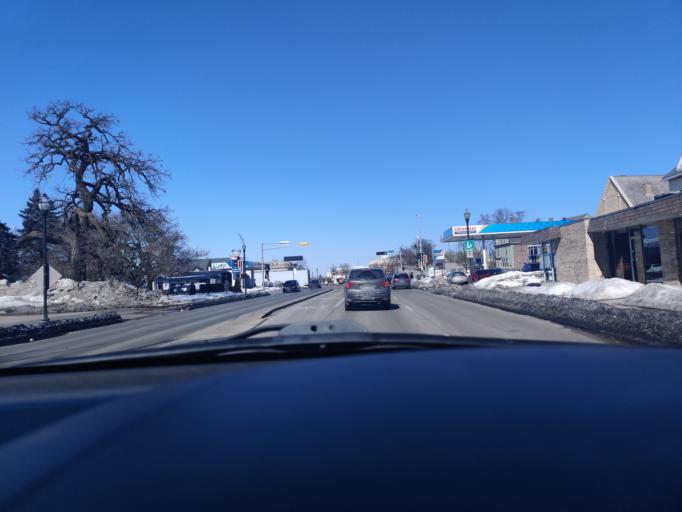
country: US
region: Wisconsin
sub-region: Kenosha County
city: Kenosha
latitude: 42.5801
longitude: -87.8215
